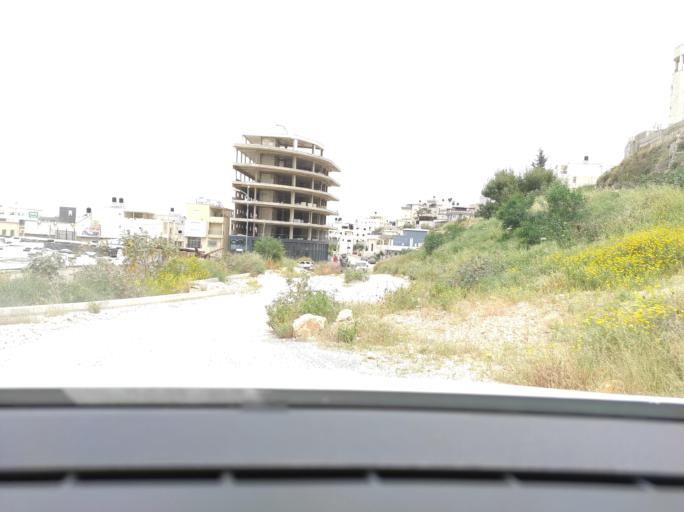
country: IL
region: Central District
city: Kafr Qasim
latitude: 32.1138
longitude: 34.9652
